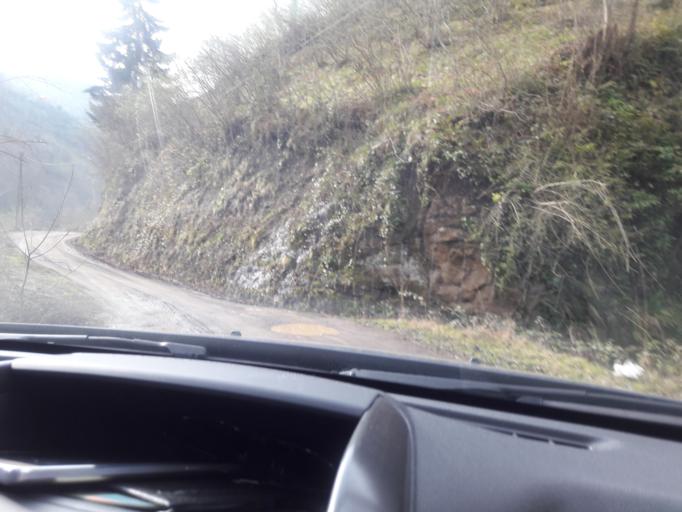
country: TR
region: Trabzon
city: Salpazari
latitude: 40.9680
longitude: 39.1953
